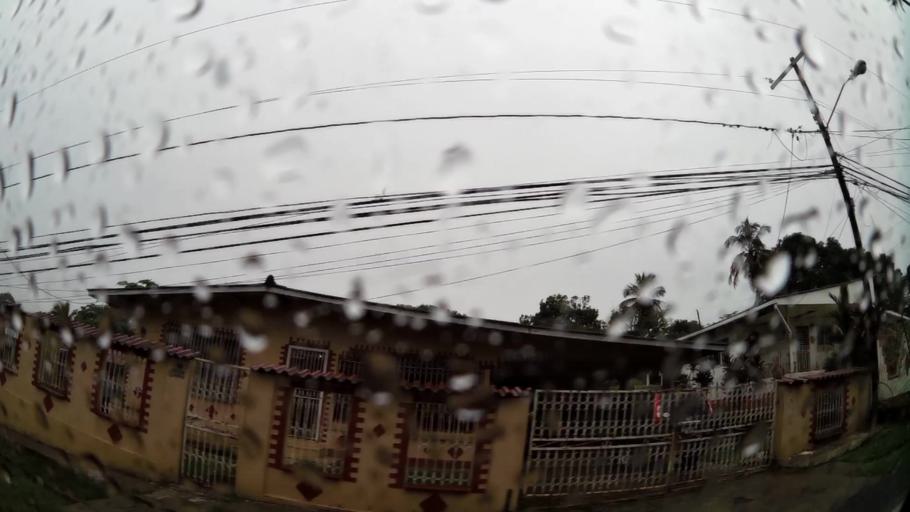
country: PA
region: Colon
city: Puerto Pilon
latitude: 9.3568
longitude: -79.8028
